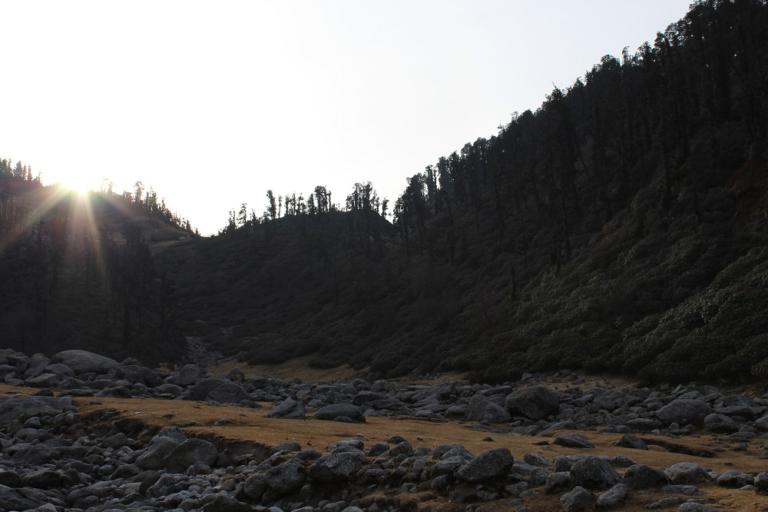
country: IN
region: Himachal Pradesh
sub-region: Kangra
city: Dharmsala
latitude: 32.3249
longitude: 76.2755
